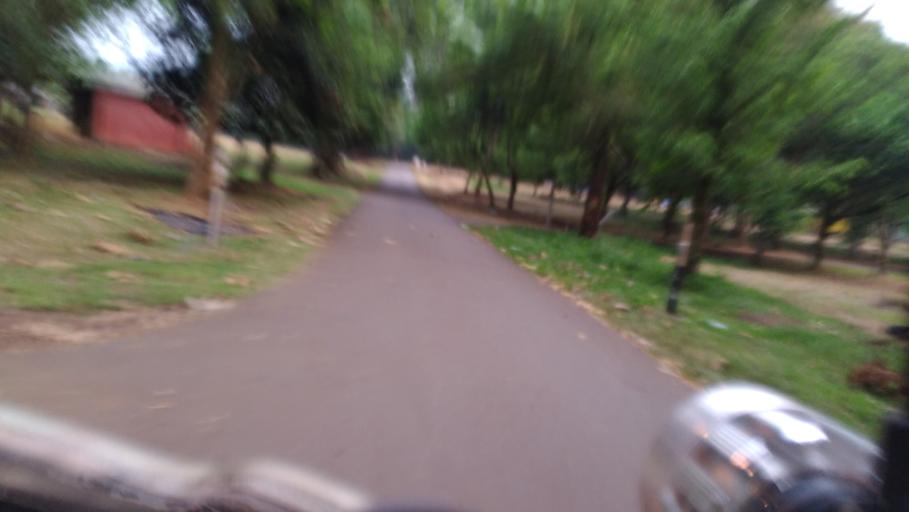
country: ID
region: West Java
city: Cileungsir
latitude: -6.3606
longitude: 106.9024
